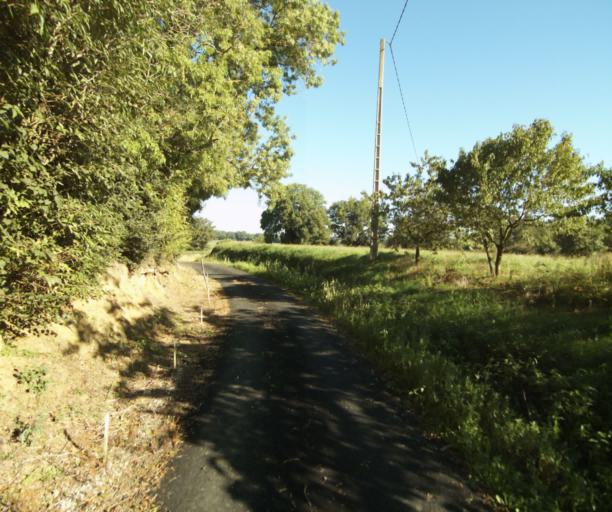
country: FR
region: Midi-Pyrenees
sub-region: Departement du Gers
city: Vic-Fezensac
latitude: 43.8264
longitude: 0.2797
